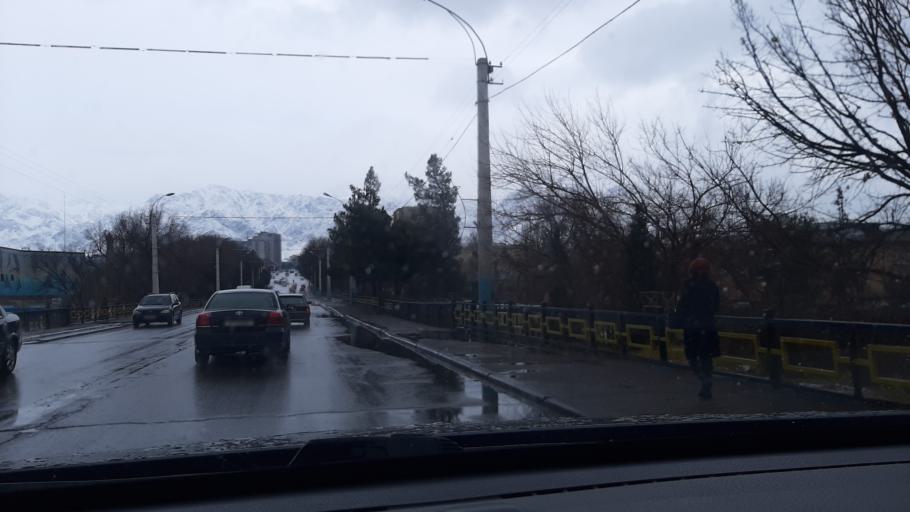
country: TJ
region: Viloyati Sughd
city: Khujand
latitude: 40.2917
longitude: 69.6194
